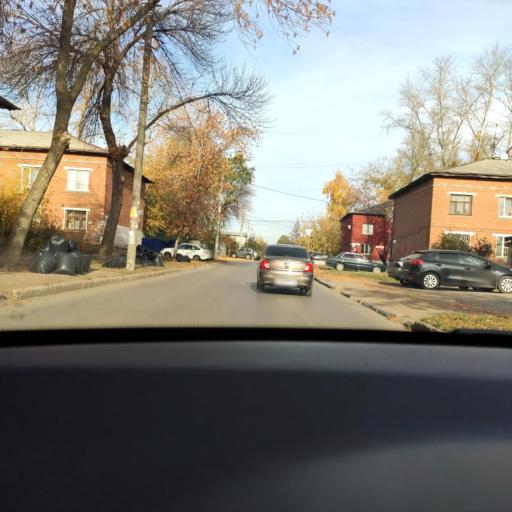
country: RU
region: Samara
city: Samara
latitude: 53.2303
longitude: 50.2382
